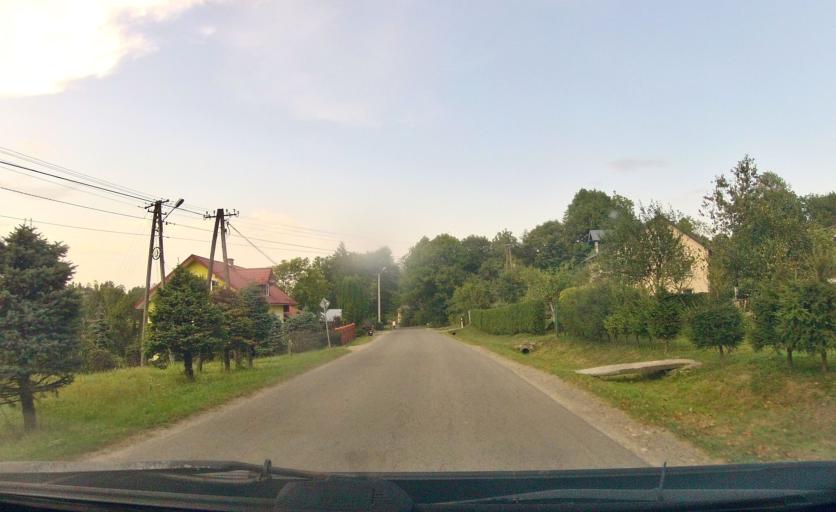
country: PL
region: Subcarpathian Voivodeship
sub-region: Powiat krosnienski
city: Dukla
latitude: 49.5474
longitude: 21.6223
